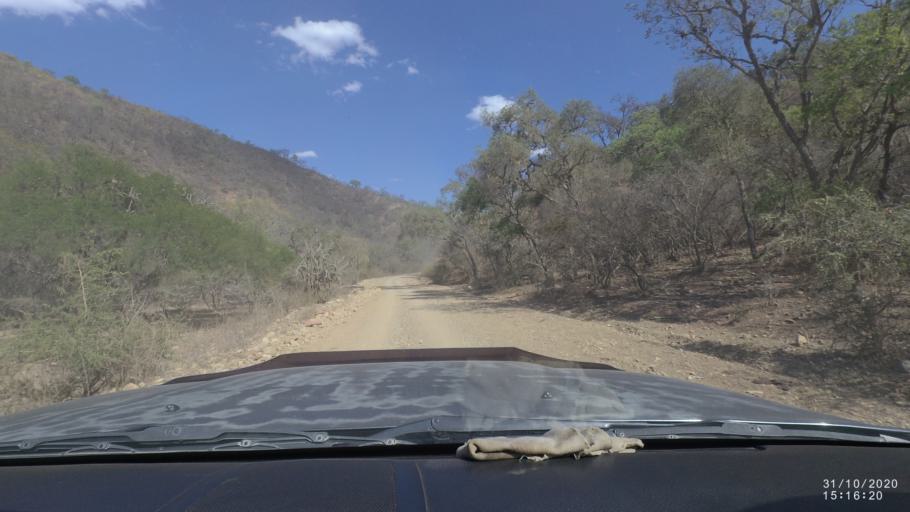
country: BO
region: Cochabamba
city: Aiquile
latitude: -18.3348
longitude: -64.7725
